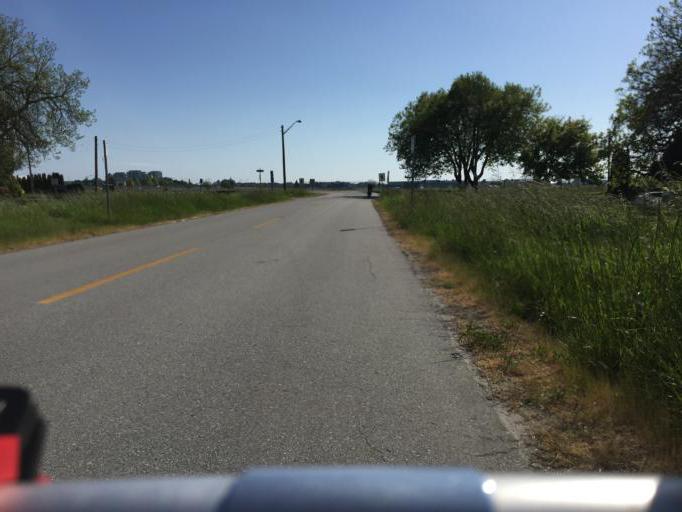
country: CA
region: British Columbia
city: Richmond
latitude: 49.1864
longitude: -123.1487
